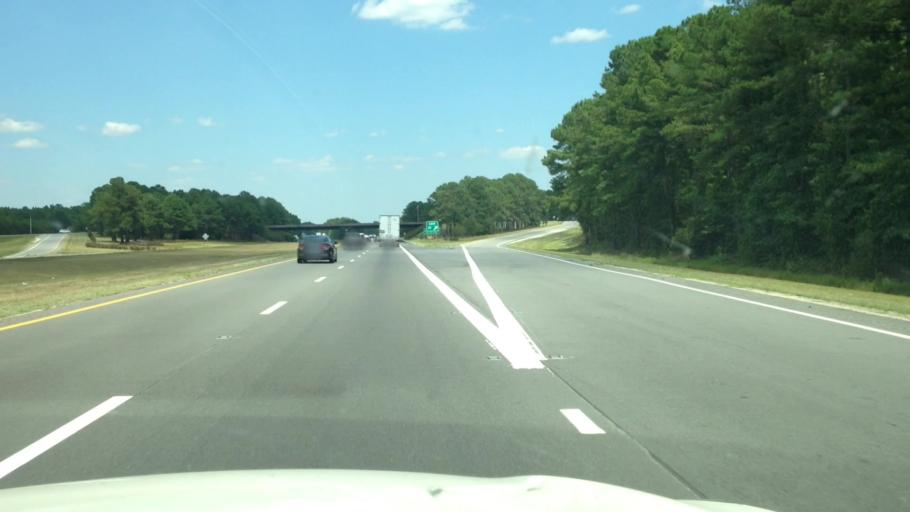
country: US
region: North Carolina
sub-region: Cumberland County
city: Hope Mills
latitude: 34.9364
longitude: -78.9267
